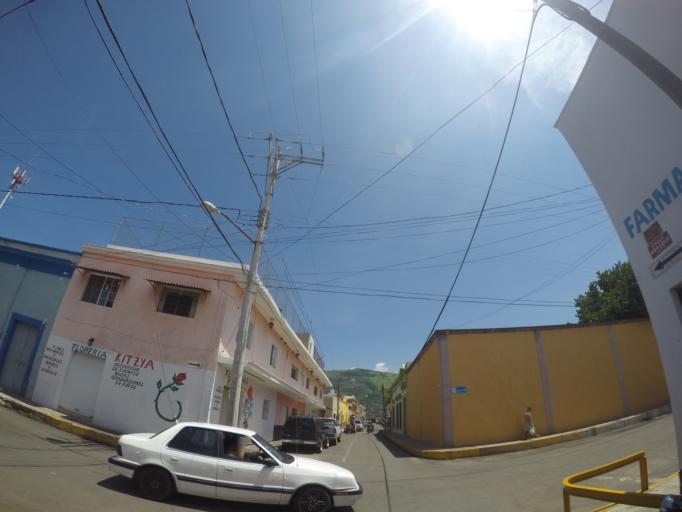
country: MX
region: Nayarit
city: Ixtlan del Rio
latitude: 21.0362
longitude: -104.3675
